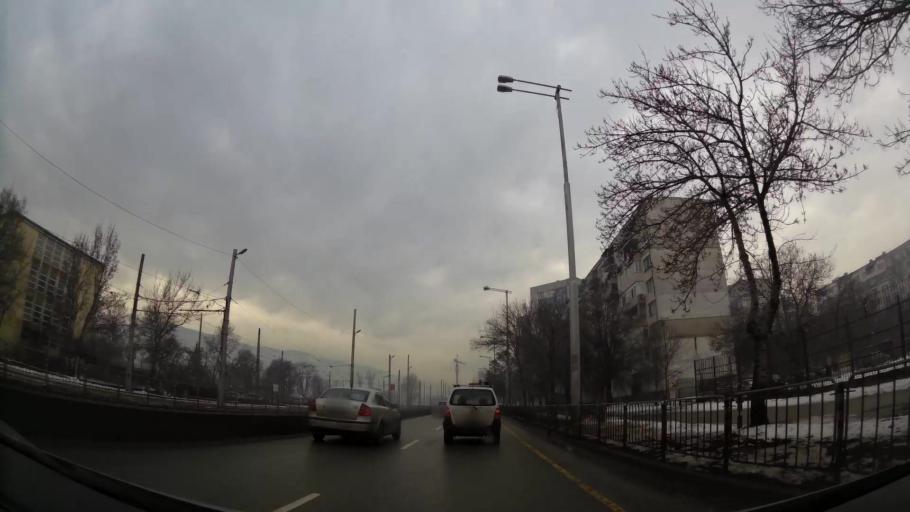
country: BG
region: Sofia-Capital
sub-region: Stolichna Obshtina
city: Sofia
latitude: 42.6926
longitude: 23.2807
